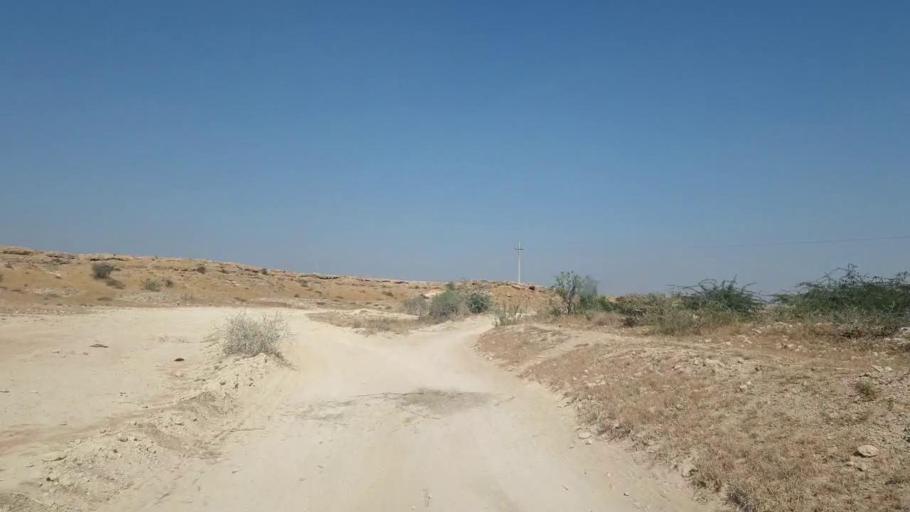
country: PK
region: Sindh
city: Thatta
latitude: 25.2174
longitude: 67.7958
